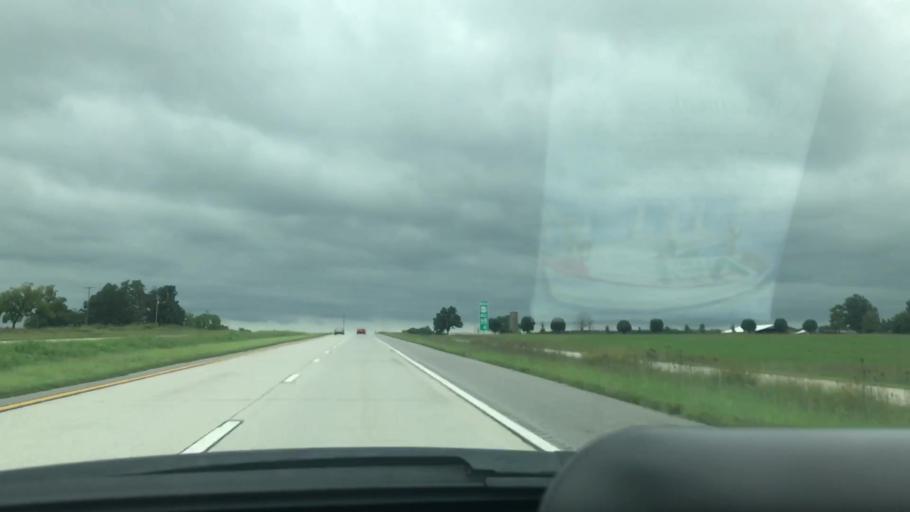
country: US
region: Missouri
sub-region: Greene County
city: Fair Grove
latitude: 37.4339
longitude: -93.1446
